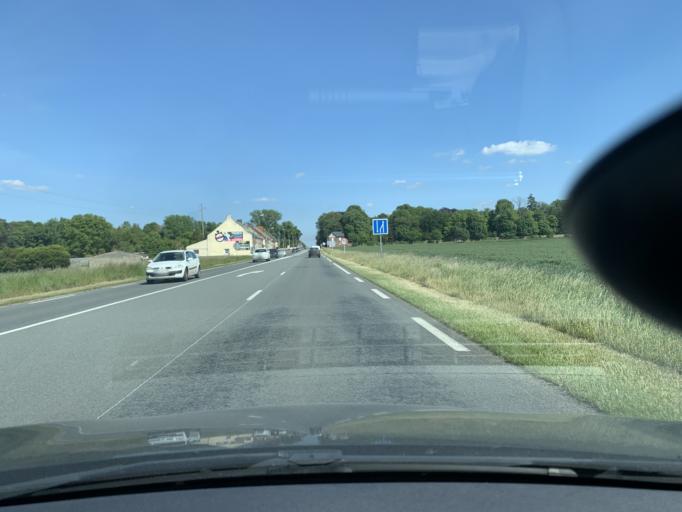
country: FR
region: Nord-Pas-de-Calais
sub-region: Departement du Nord
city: Fontaine-au-Pire
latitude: 50.1508
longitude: 3.3388
